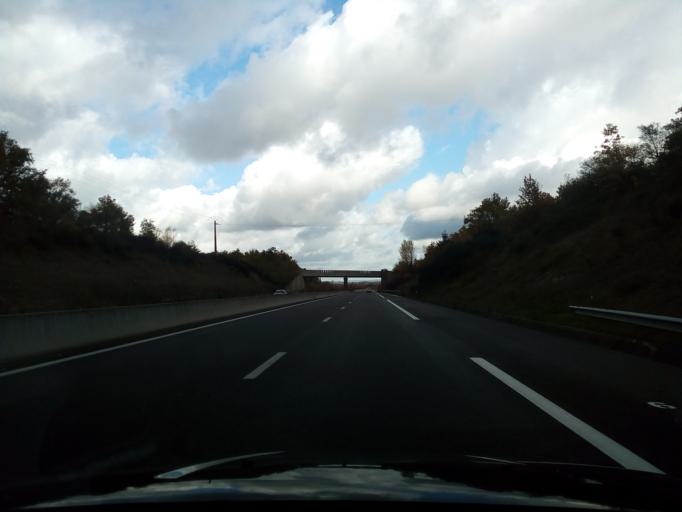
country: FR
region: Auvergne
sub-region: Departement de l'Allier
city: Domerat
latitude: 46.3516
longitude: 2.5447
